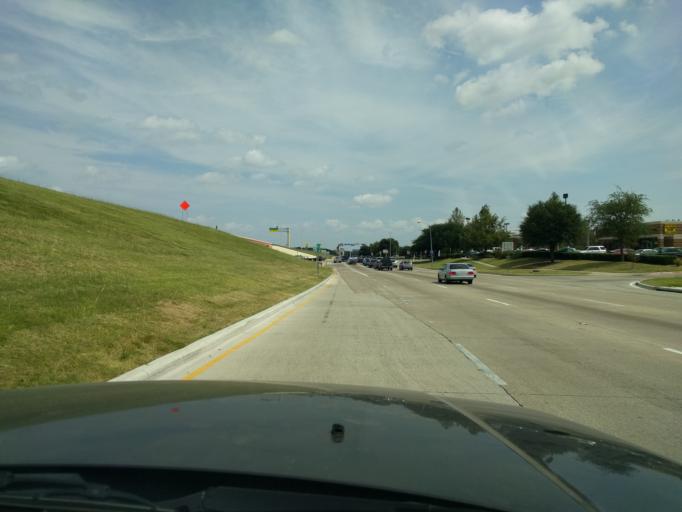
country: US
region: Texas
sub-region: Collin County
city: Plano
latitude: 33.0022
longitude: -96.6842
